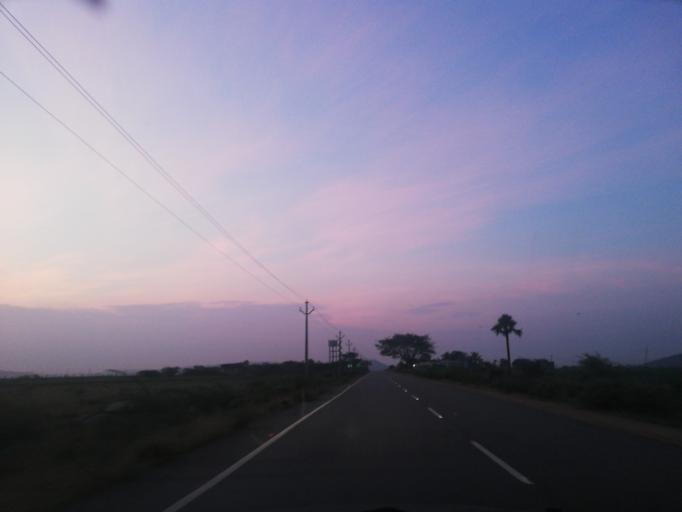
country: IN
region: Andhra Pradesh
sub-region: Guntur
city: Macherla
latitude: 16.6911
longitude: 79.2492
